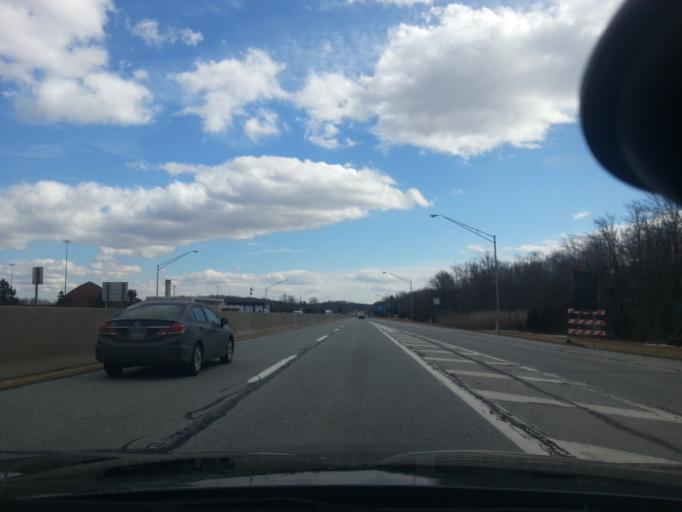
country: US
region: Pennsylvania
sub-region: Bucks County
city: Spinnerstown
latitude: 40.4376
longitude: -75.4260
